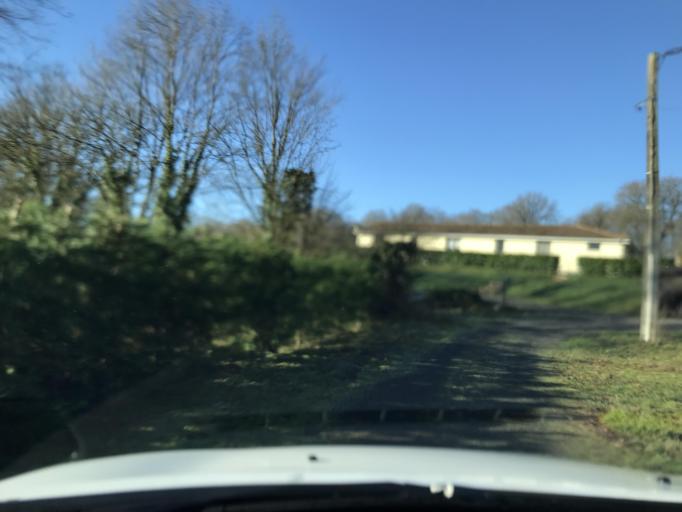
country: FR
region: Poitou-Charentes
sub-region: Departement de la Charente
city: Chasseneuil-sur-Bonnieure
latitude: 45.8367
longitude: 0.4927
